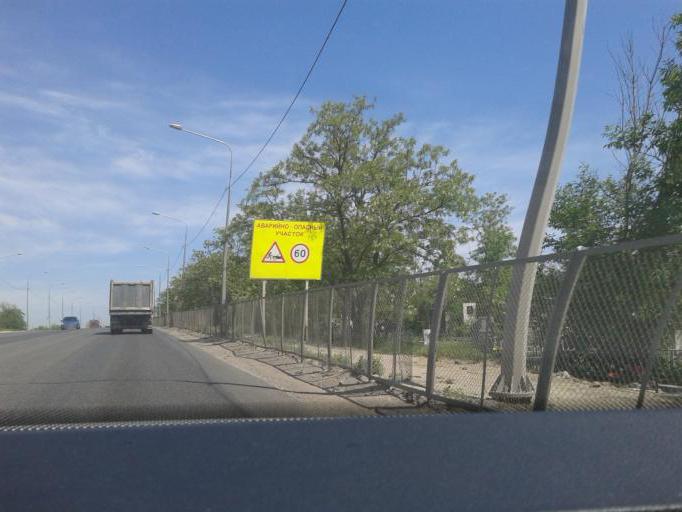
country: RU
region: Volgograd
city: Gorodishche
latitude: 48.7822
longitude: 44.5202
